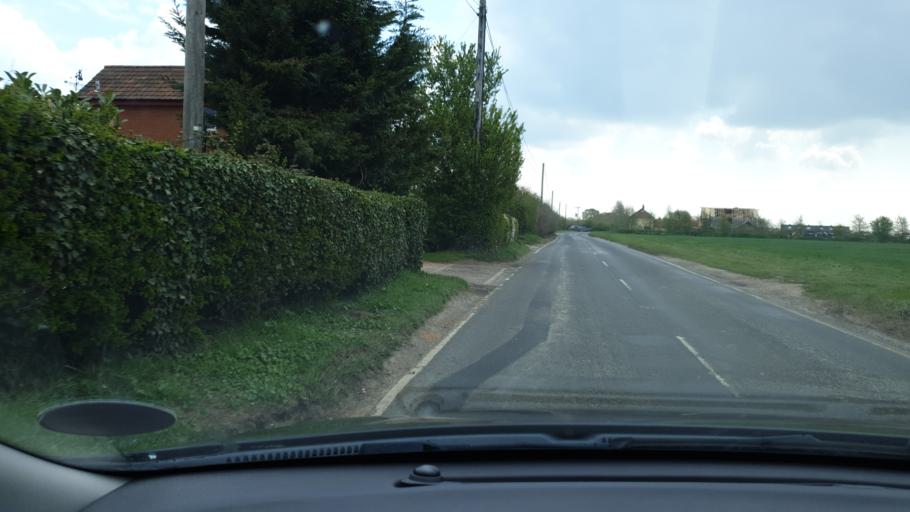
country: GB
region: England
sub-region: Essex
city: Alresford
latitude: 51.9029
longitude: 1.0106
